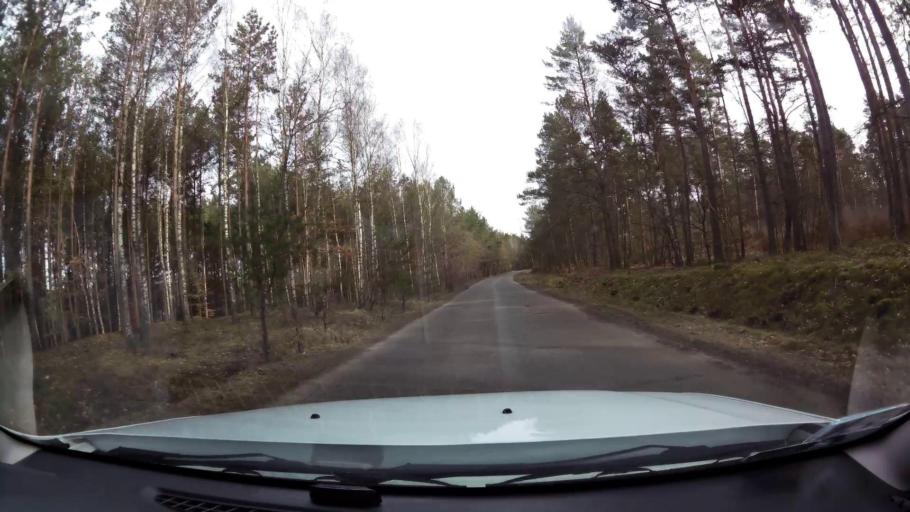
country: PL
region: West Pomeranian Voivodeship
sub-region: Powiat stargardzki
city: Insko
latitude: 53.4664
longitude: 15.6792
